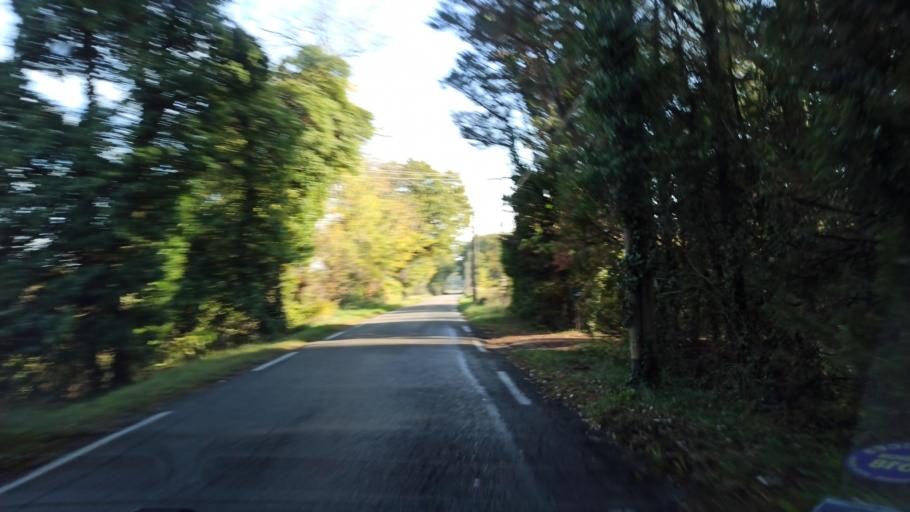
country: FR
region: Provence-Alpes-Cote d'Azur
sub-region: Departement du Vaucluse
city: Goult
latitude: 43.8464
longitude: 5.2465
